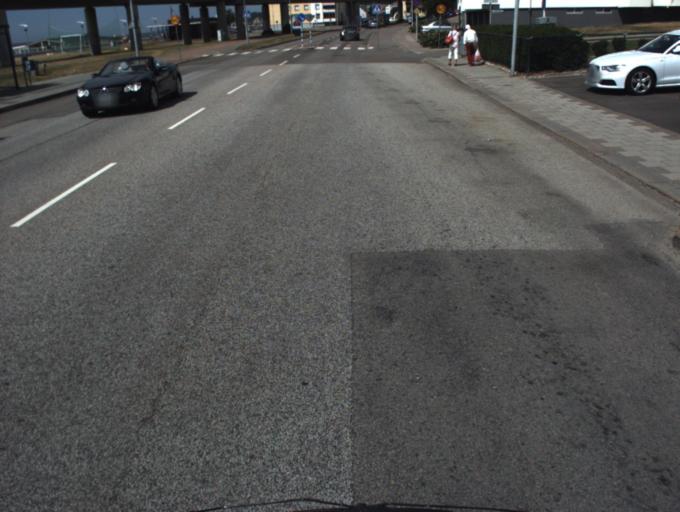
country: SE
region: Skane
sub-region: Helsingborg
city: Helsingborg
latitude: 56.0575
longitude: 12.6832
